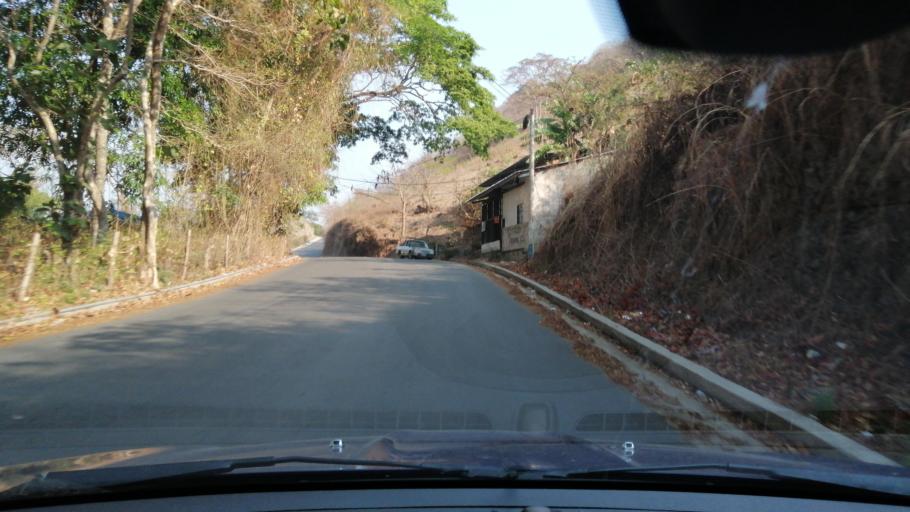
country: SV
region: Santa Ana
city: Texistepeque
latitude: 14.2257
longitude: -89.4554
